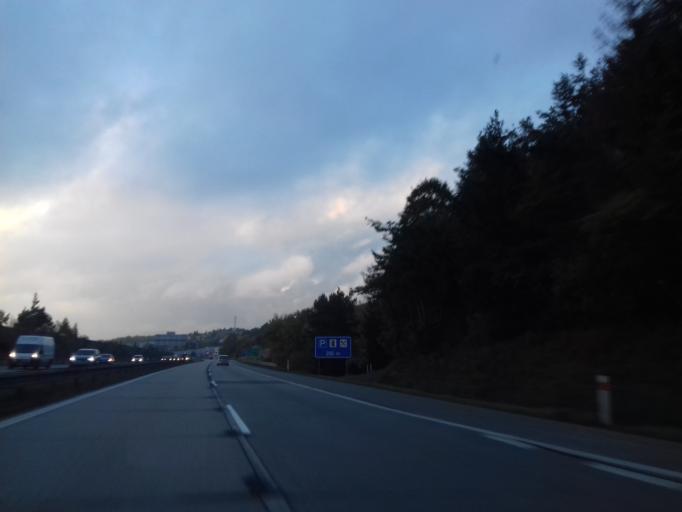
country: CZ
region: Vysocina
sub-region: Okres Zd'ar nad Sazavou
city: Velke Mezirici
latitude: 49.3495
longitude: 16.0377
